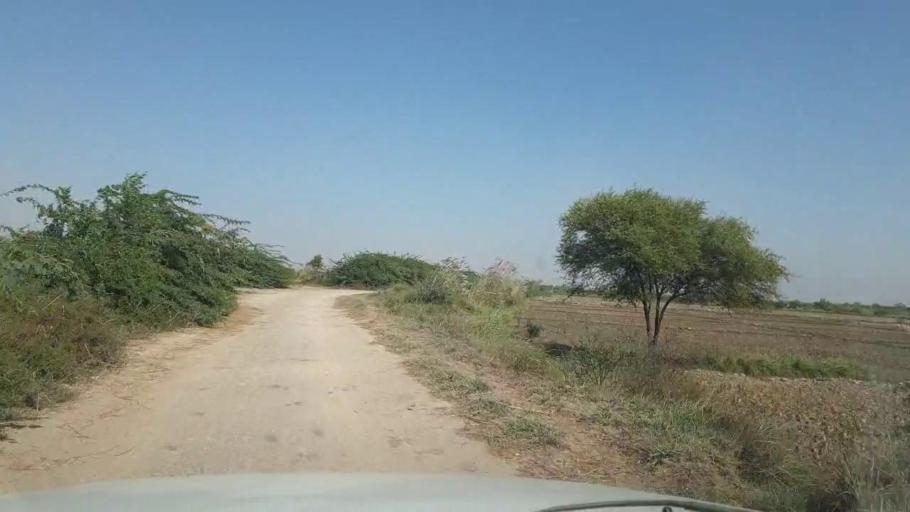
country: PK
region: Sindh
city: Mirpur Sakro
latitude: 24.4039
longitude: 67.7488
